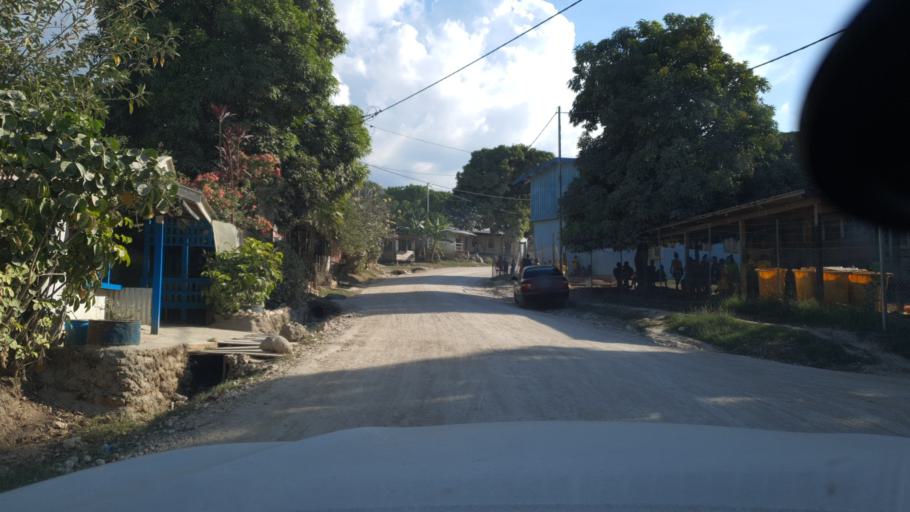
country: SB
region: Guadalcanal
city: Honiara
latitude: -9.4529
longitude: 159.9916
